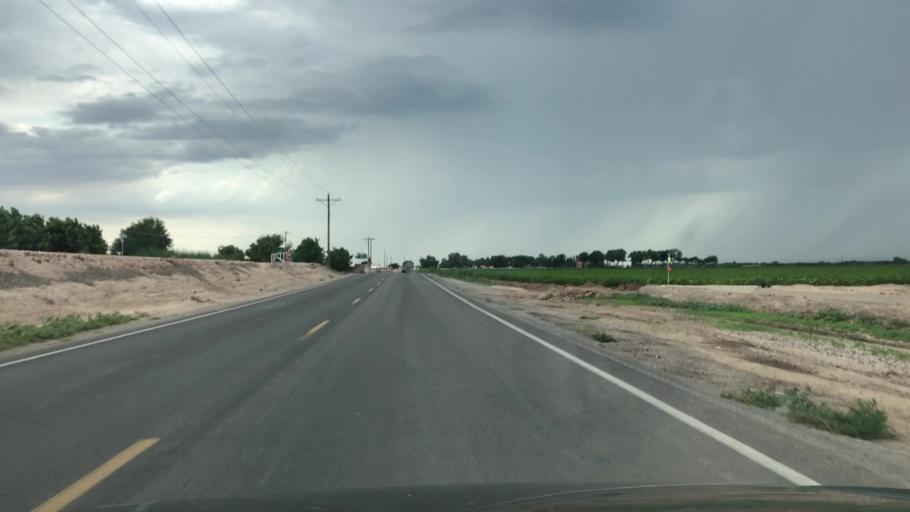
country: US
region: New Mexico
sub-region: Dona Ana County
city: Anthony
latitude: 32.0208
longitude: -106.6698
